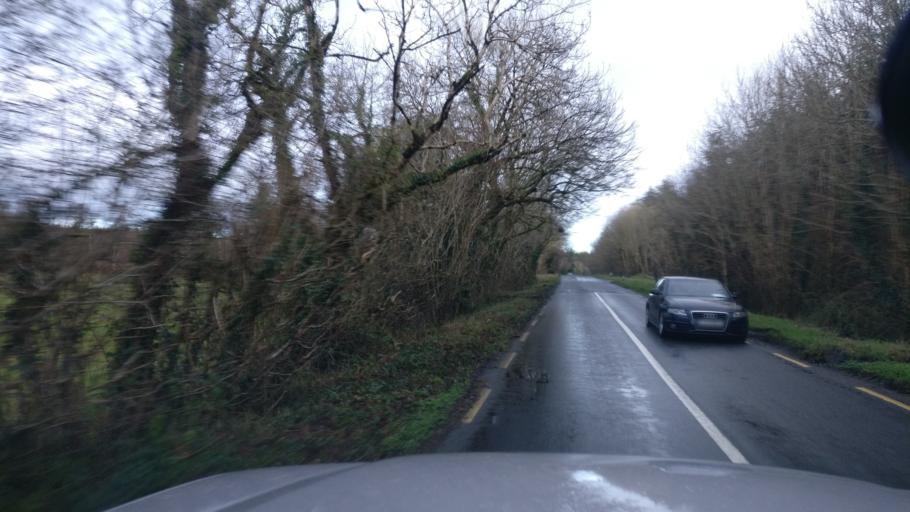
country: IE
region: Connaught
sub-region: County Galway
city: Athenry
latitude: 53.2970
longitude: -8.6642
